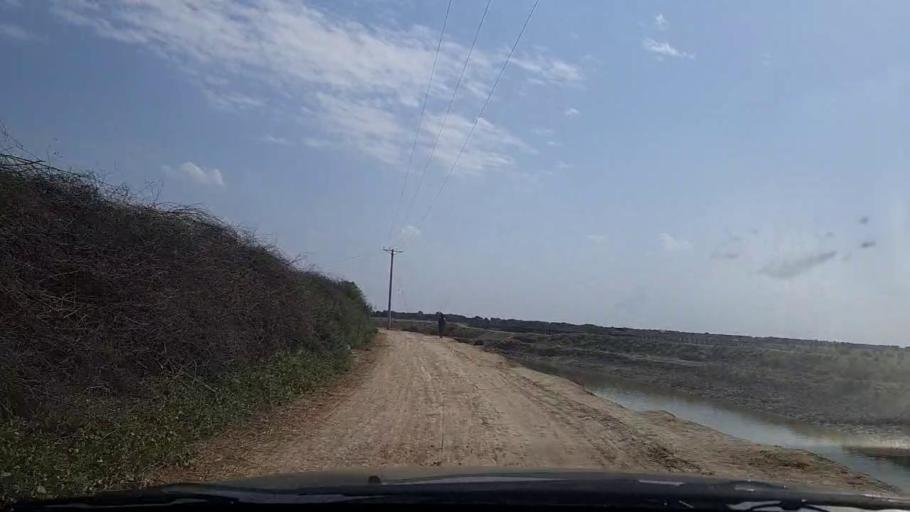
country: PK
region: Sindh
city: Mirpur Batoro
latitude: 24.5686
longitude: 68.1977
